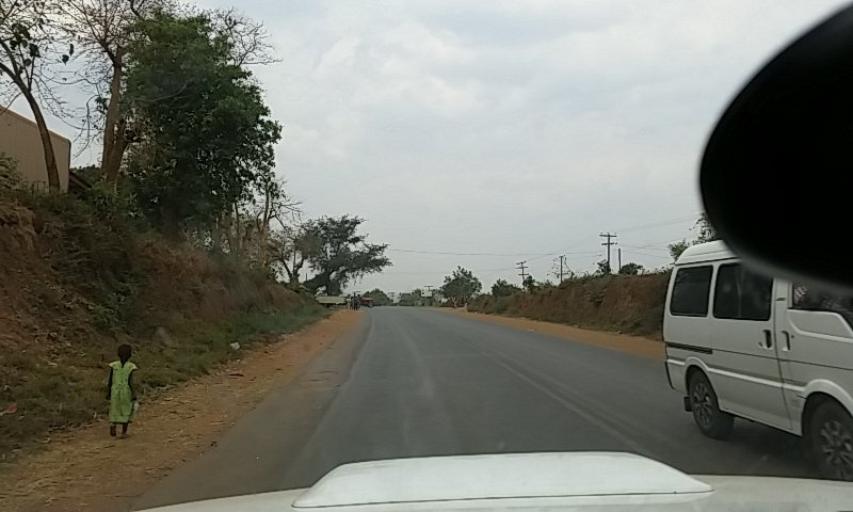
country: MW
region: Central Region
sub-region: Lilongwe District
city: Lilongwe
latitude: -13.9013
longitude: 33.8015
